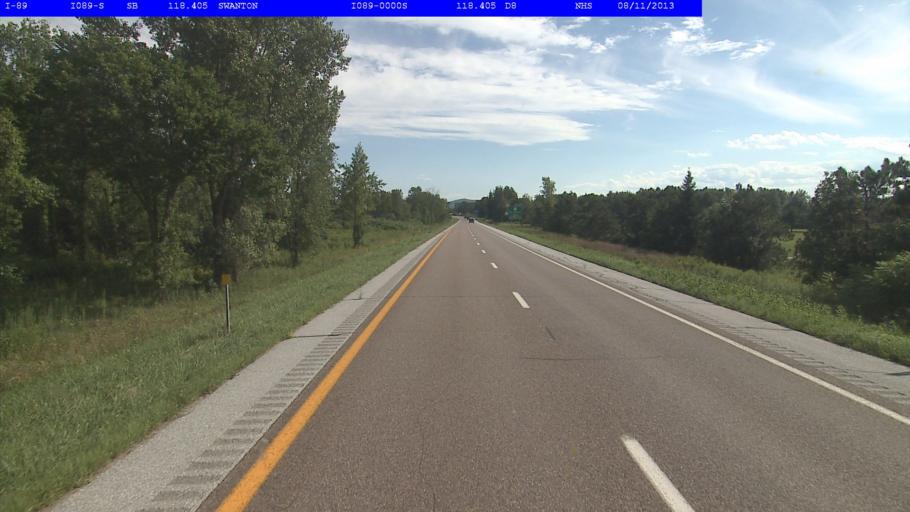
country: US
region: Vermont
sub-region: Franklin County
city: Saint Albans
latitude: 44.8540
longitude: -73.0827
